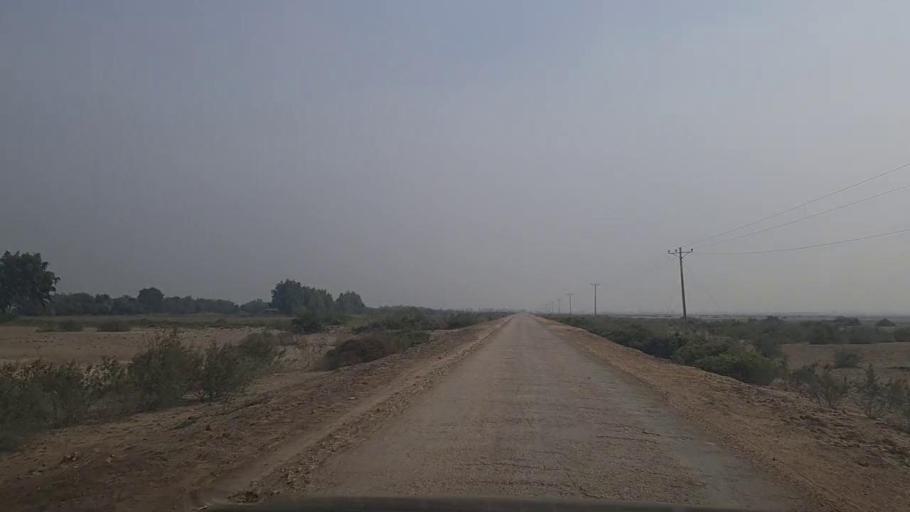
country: PK
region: Sindh
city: Mirpur Sakro
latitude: 24.4611
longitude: 67.6935
